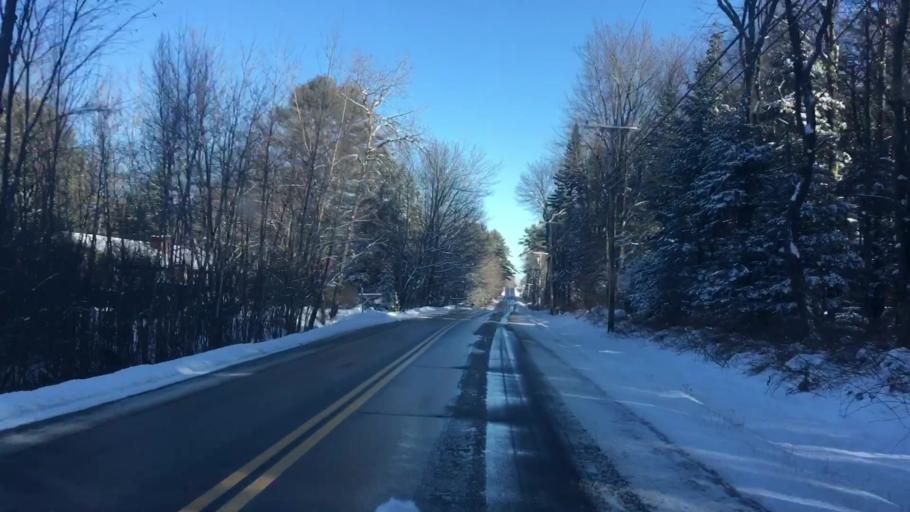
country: US
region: Maine
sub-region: Androscoggin County
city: Lisbon Falls
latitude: 43.9484
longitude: -70.1160
